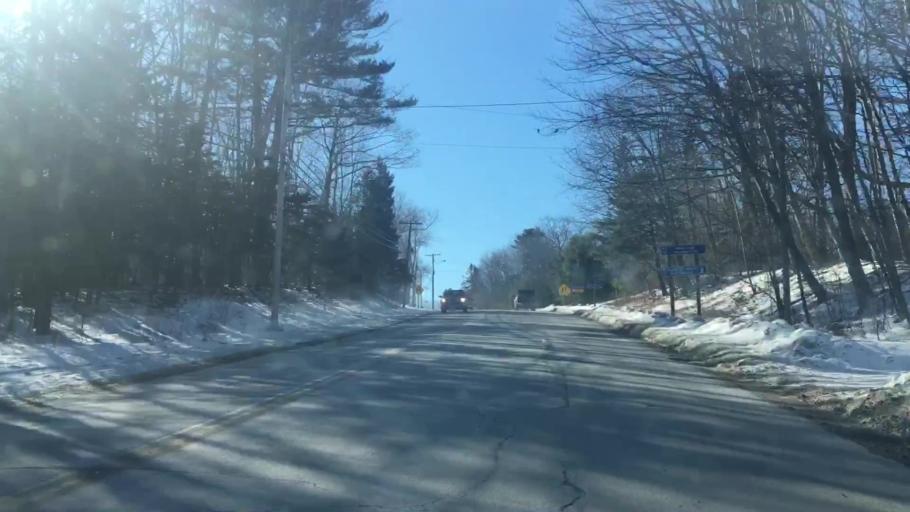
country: US
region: Maine
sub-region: Hancock County
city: Sedgwick
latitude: 44.4104
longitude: -68.5943
